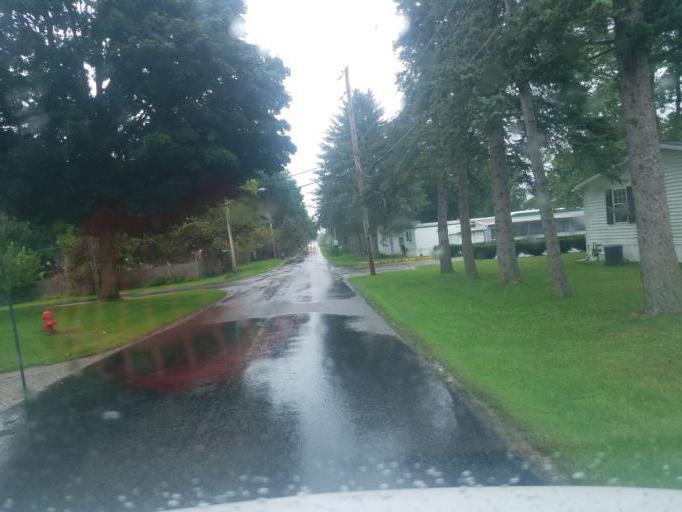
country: US
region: Ohio
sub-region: Wayne County
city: Creston
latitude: 40.9815
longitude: -81.9095
